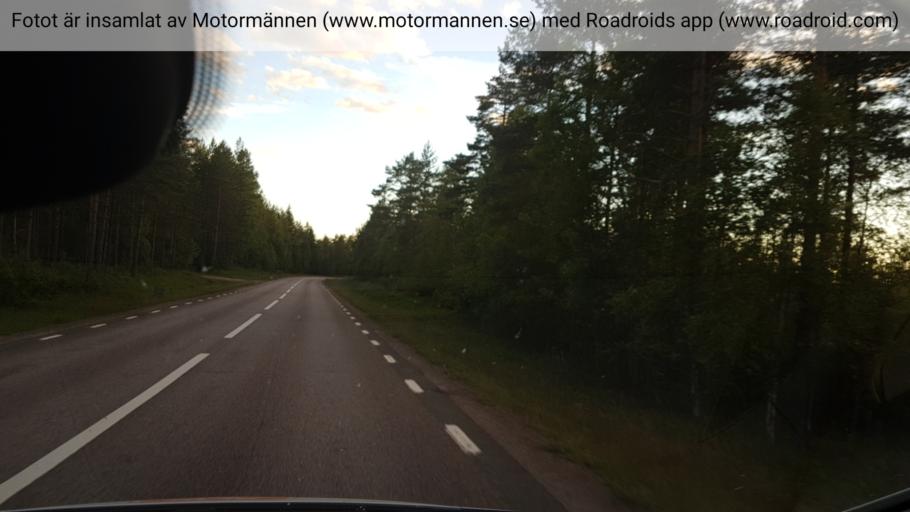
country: SE
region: Vaermland
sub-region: Sunne Kommun
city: Sunne
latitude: 59.6953
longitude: 13.0916
